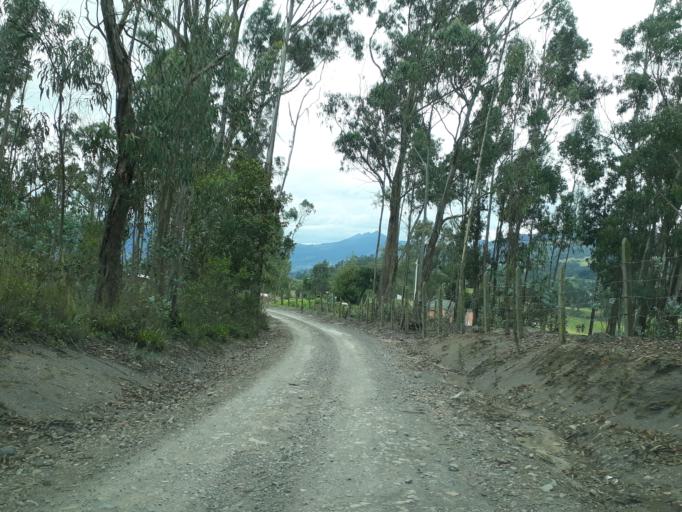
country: CO
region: Boyaca
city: Chiquinquira
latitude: 5.5652
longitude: -73.8101
